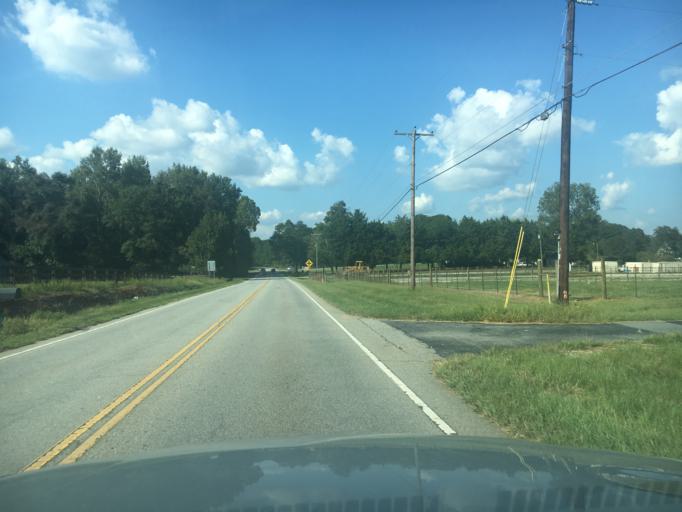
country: US
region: South Carolina
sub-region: Greenville County
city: Fountain Inn
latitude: 34.6522
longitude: -82.2574
